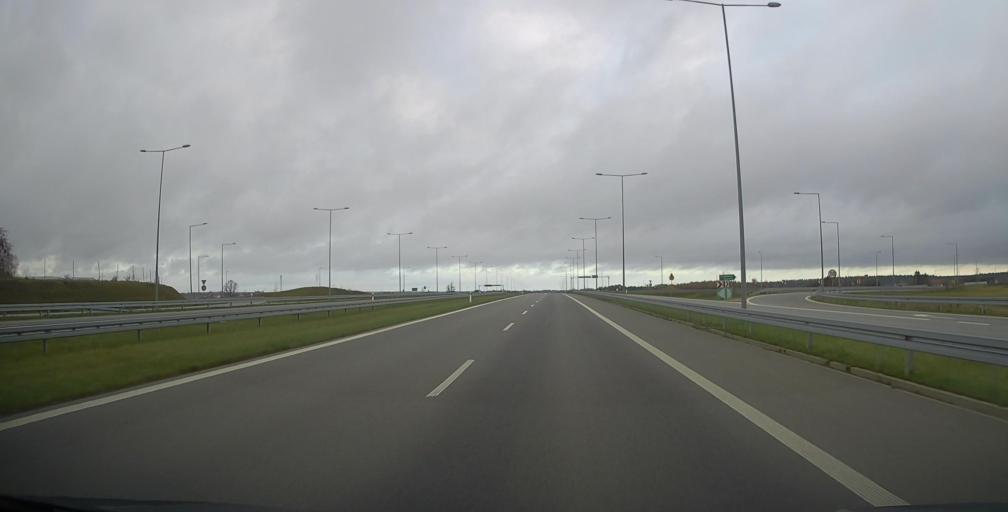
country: PL
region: Podlasie
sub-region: Powiat suwalski
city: Raczki
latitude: 53.9684
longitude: 22.7827
